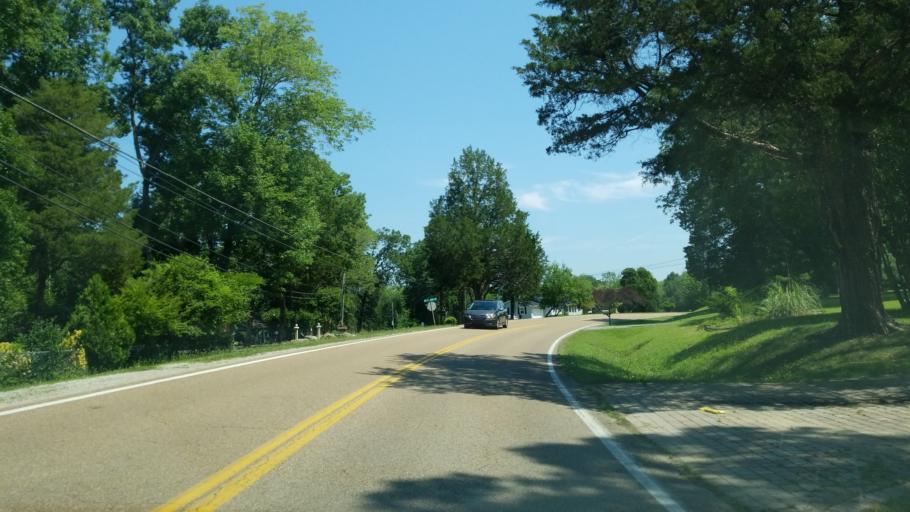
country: US
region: Tennessee
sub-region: Hamilton County
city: Collegedale
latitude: 35.1113
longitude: -85.0467
